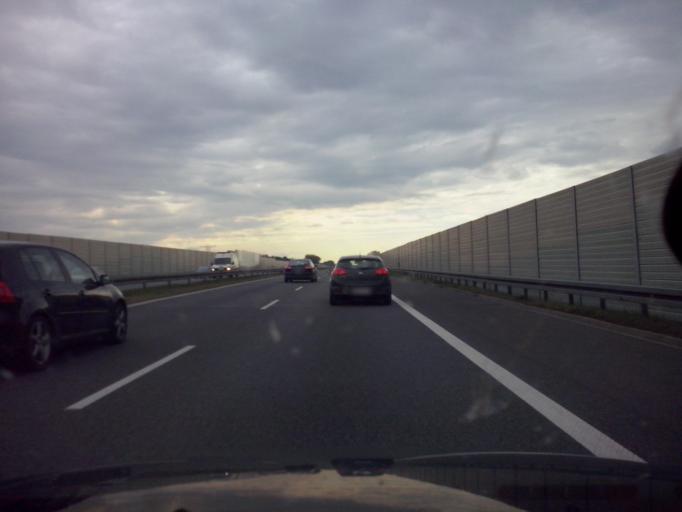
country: PL
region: Lesser Poland Voivodeship
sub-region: Powiat wielicki
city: Wegrzce Wielkie
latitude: 50.0184
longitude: 20.1154
